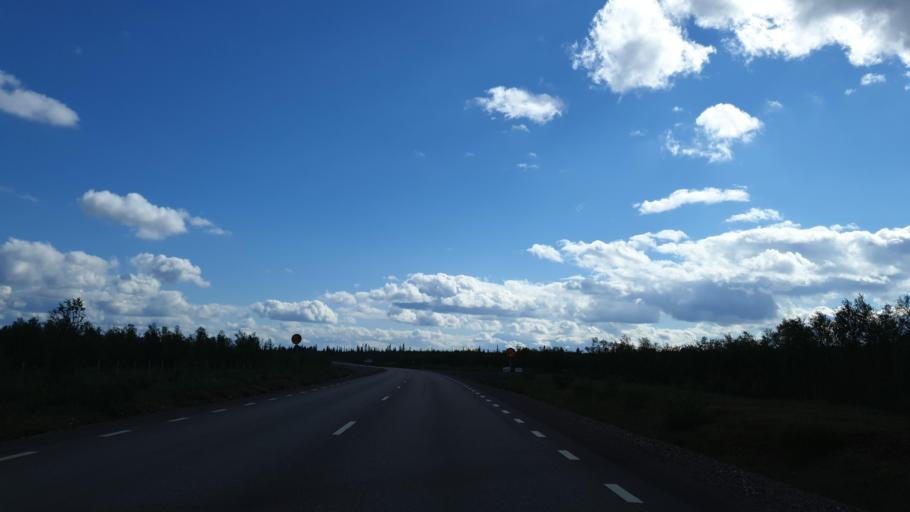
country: SE
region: Norrbotten
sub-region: Kiruna Kommun
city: Kiruna
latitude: 67.8115
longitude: 20.2369
